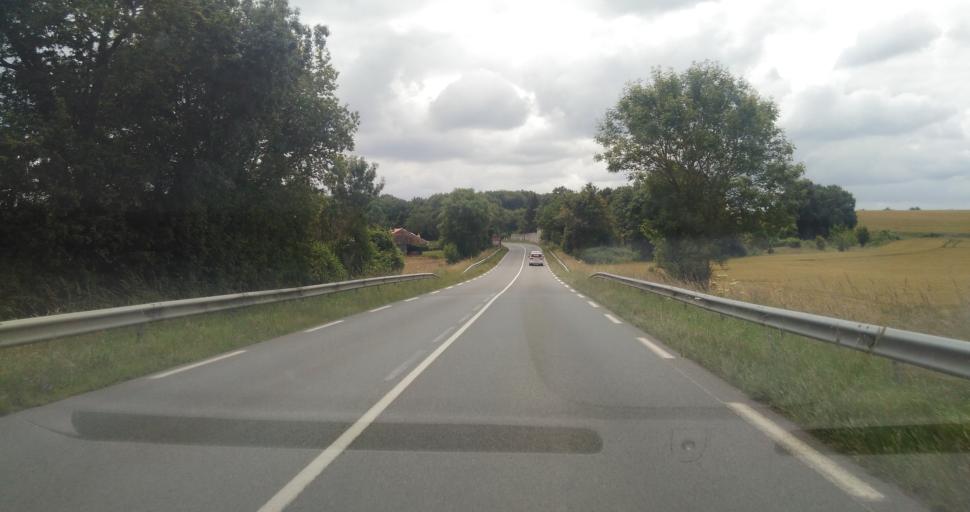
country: FR
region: Pays de la Loire
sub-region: Departement de la Vendee
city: Sainte-Hermine
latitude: 46.5885
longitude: -1.1165
